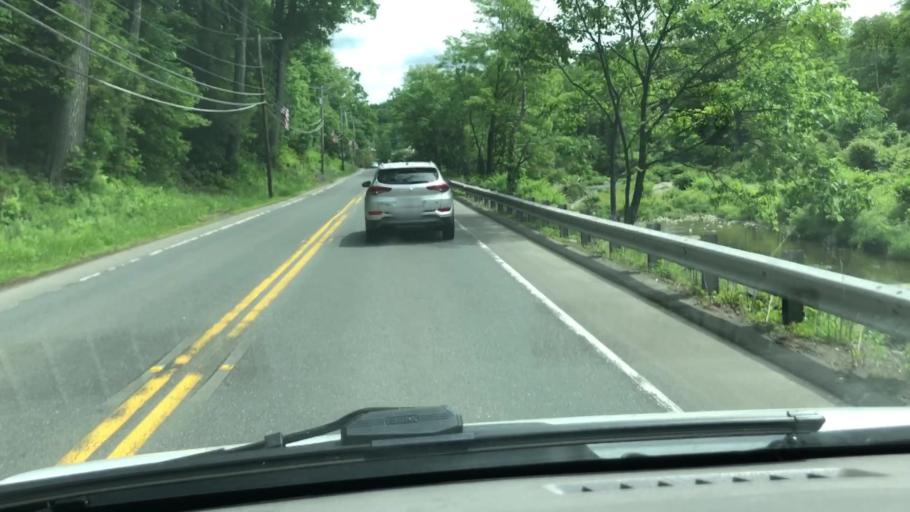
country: US
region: Massachusetts
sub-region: Hampshire County
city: Williamsburg
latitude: 42.3791
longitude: -72.7066
